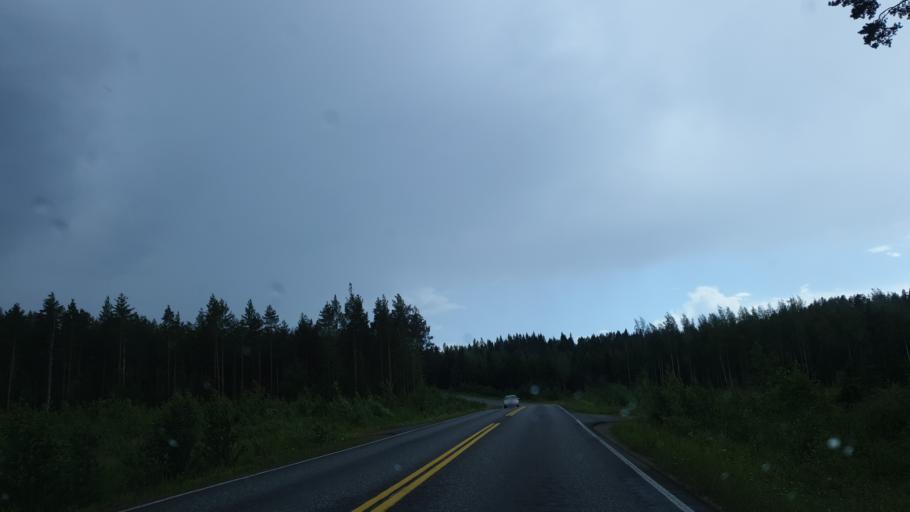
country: FI
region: Northern Savo
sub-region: Kuopio
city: Vehmersalmi
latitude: 62.9343
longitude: 27.9124
